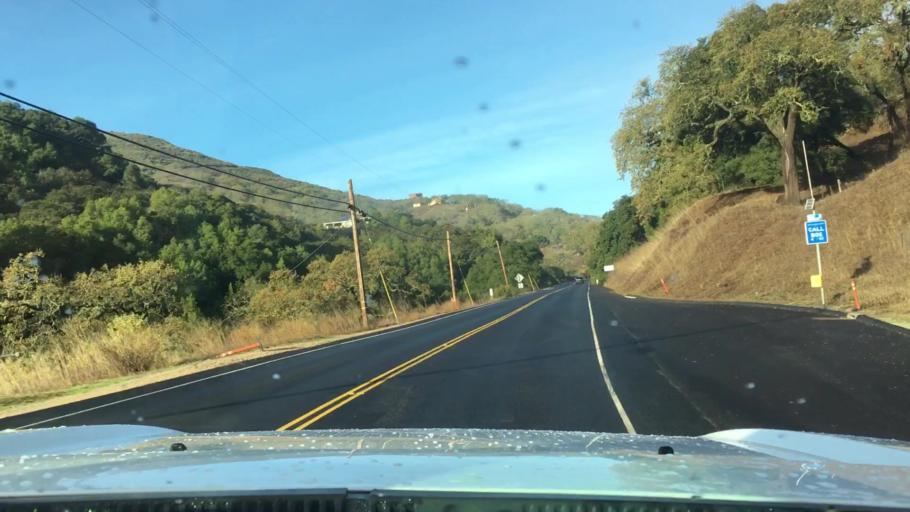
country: US
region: California
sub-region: San Luis Obispo County
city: Atascadero
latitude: 35.4511
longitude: -120.7039
